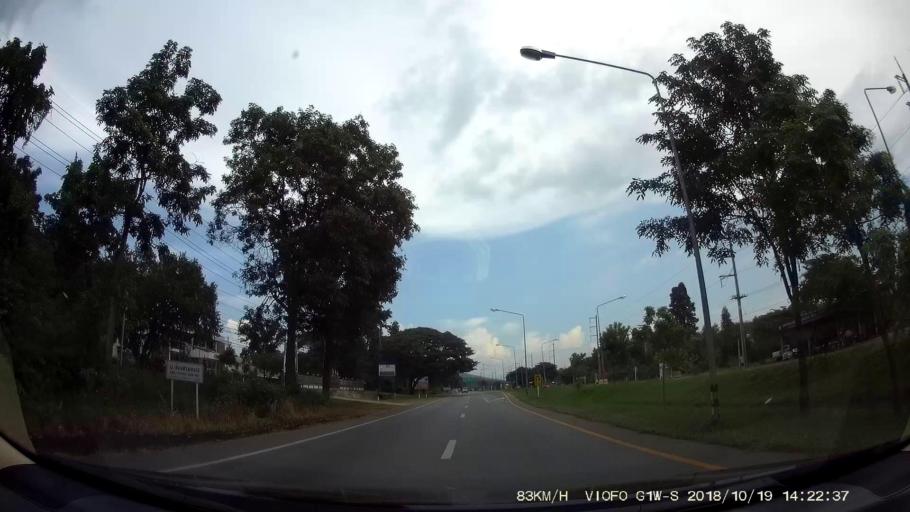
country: TH
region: Chaiyaphum
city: Kaeng Khro
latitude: 16.0647
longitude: 102.2762
